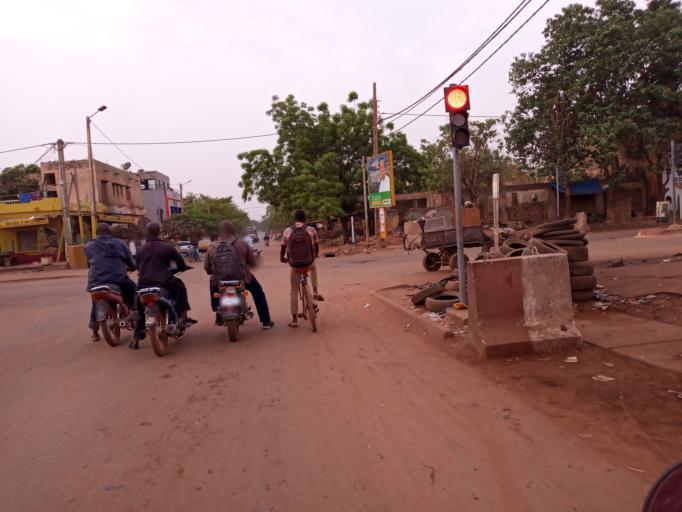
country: ML
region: Bamako
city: Bamako
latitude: 12.6633
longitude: -7.9731
